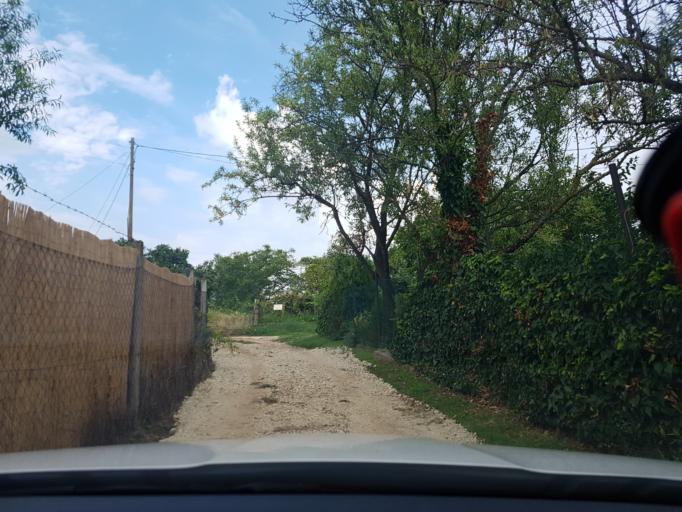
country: HU
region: Veszprem
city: Balatonalmadi
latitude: 46.9932
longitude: 17.9822
